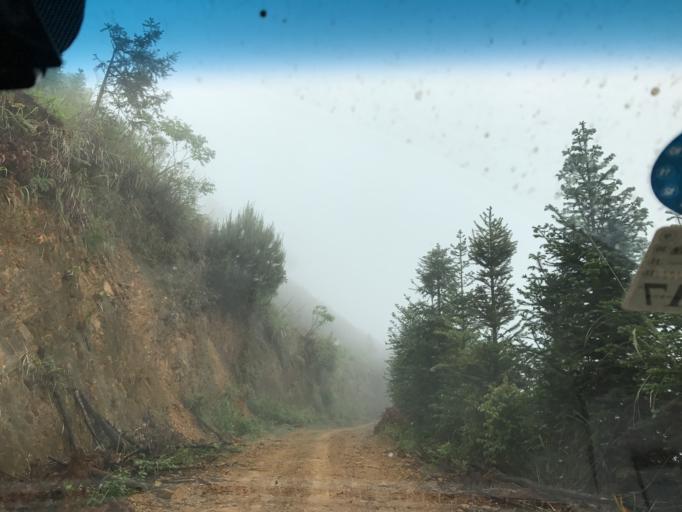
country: CN
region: Guangxi Zhuangzu Zizhiqu
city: Leli
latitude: 24.8097
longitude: 106.0786
